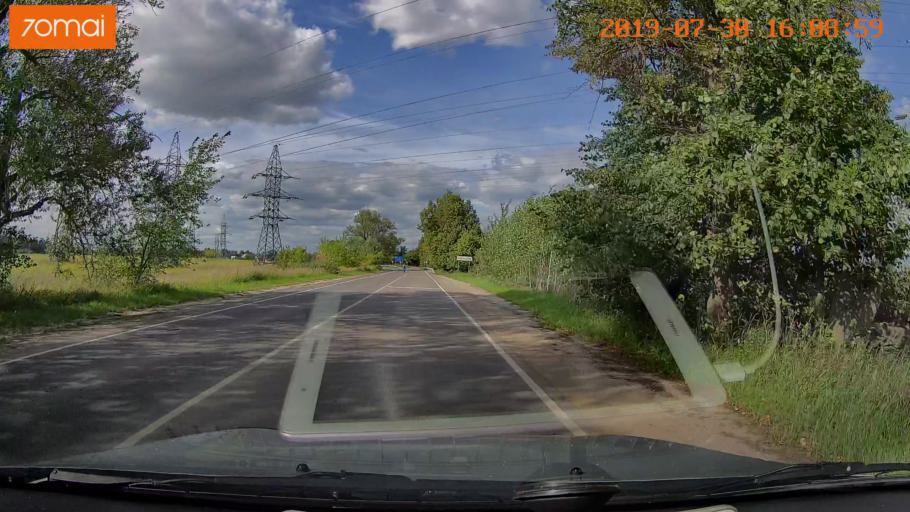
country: RU
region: Moskovskaya
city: Peski
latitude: 55.2499
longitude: 38.7194
